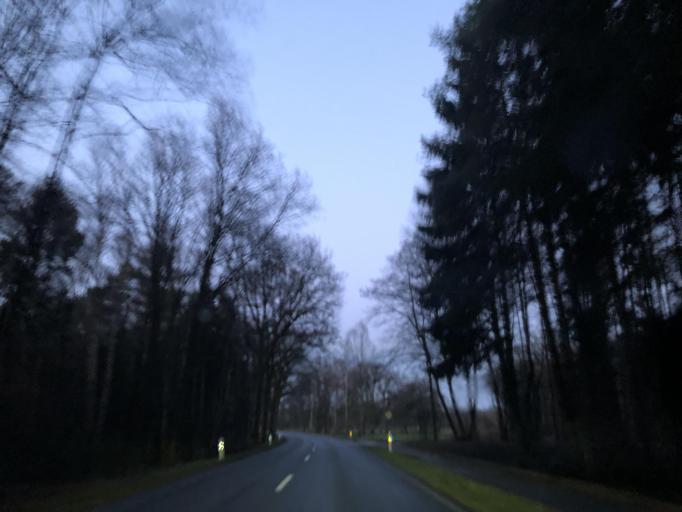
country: DE
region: Lower Saxony
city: Wietzendorf
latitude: 52.9148
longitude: 9.9387
